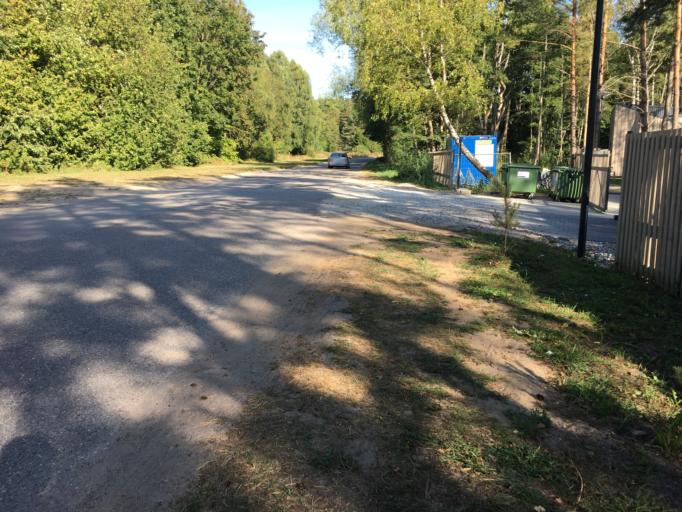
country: LT
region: Klaipedos apskritis
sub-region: Klaipeda
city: Palanga
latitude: 55.9480
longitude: 21.0765
